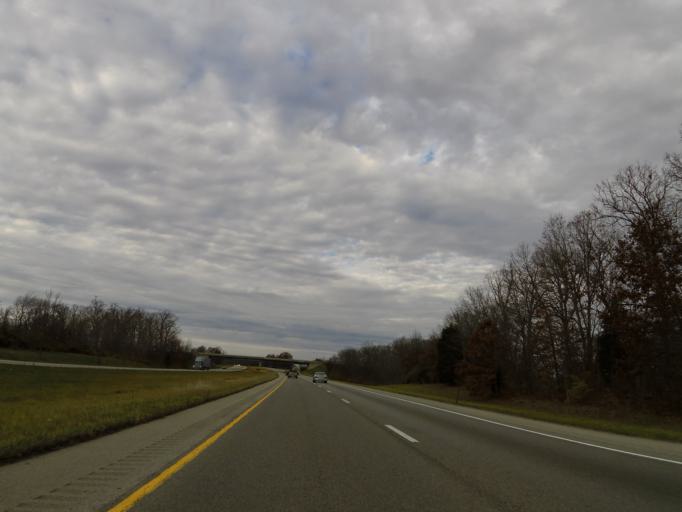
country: US
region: Illinois
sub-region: Clinton County
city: Wamac
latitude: 38.3847
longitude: -89.1237
